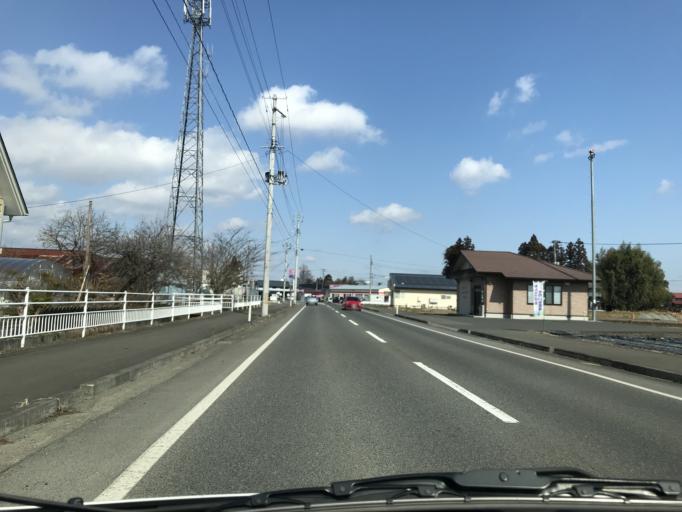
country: JP
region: Iwate
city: Mizusawa
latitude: 39.1259
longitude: 141.1492
